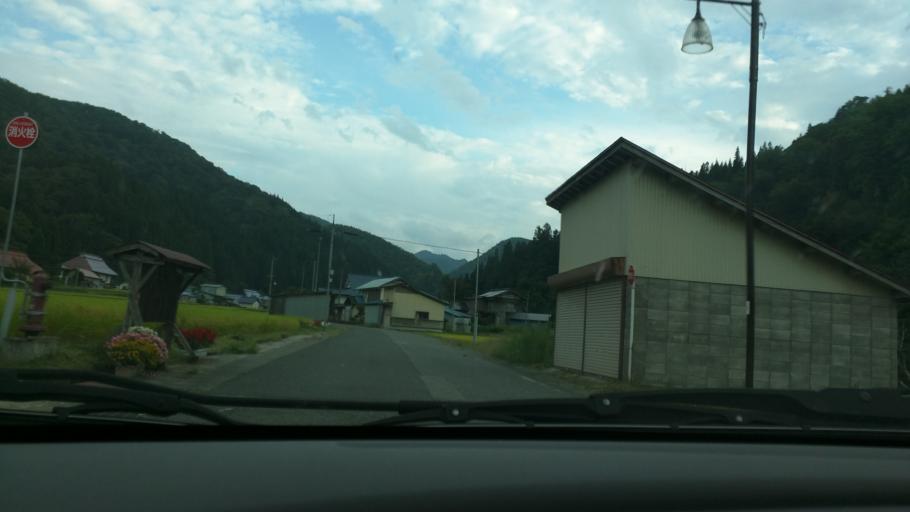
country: JP
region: Fukushima
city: Kitakata
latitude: 37.4497
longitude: 139.6499
